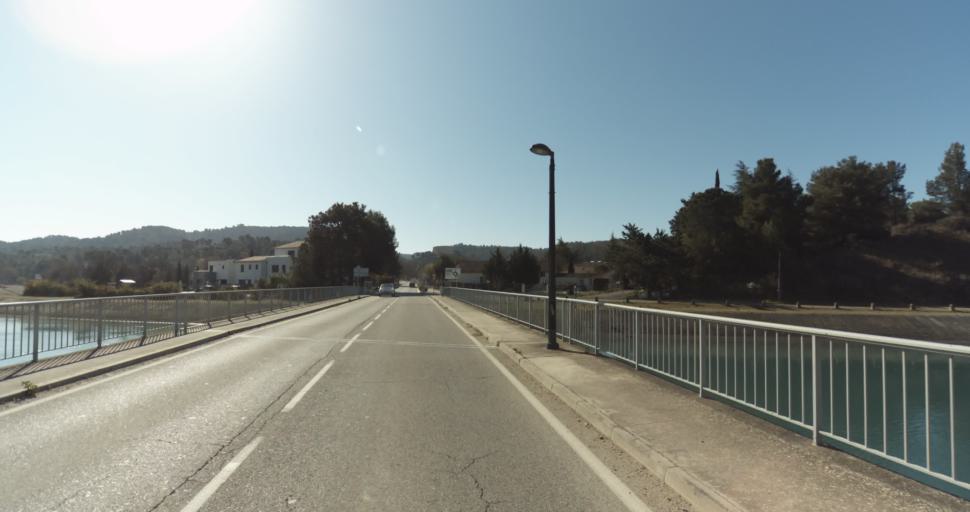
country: FR
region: Provence-Alpes-Cote d'Azur
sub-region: Departement des Bouches-du-Rhone
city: Meyrargues
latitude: 43.6425
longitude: 5.5238
